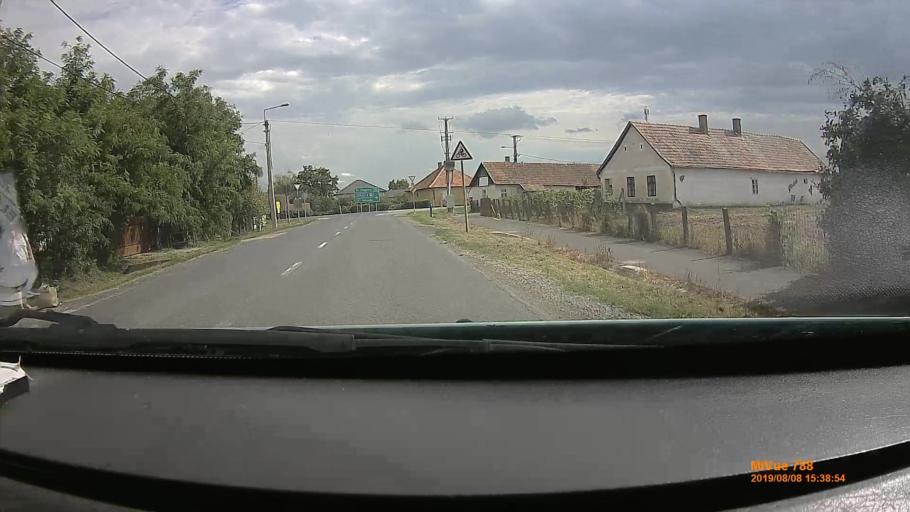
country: HU
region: Szabolcs-Szatmar-Bereg
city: Kocsord
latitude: 47.9389
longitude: 22.4287
